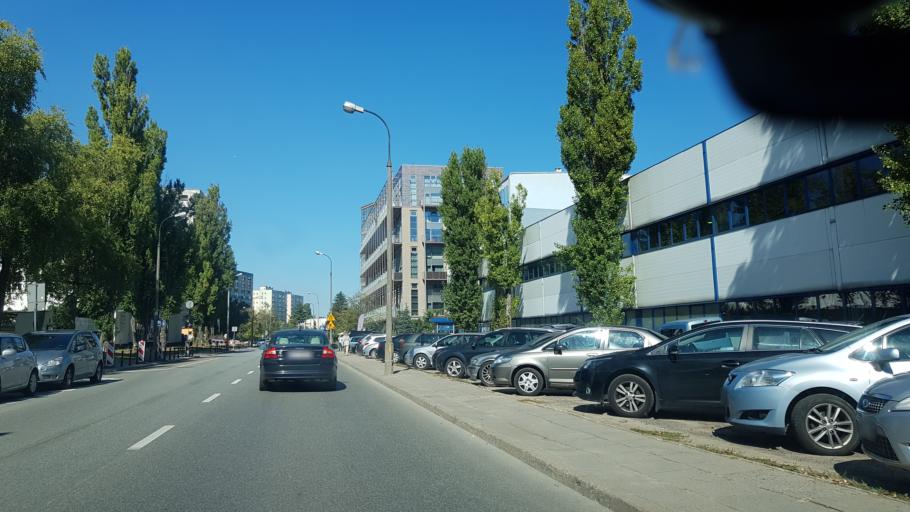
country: PL
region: Masovian Voivodeship
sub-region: Warszawa
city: Ochota
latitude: 52.1866
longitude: 20.9930
